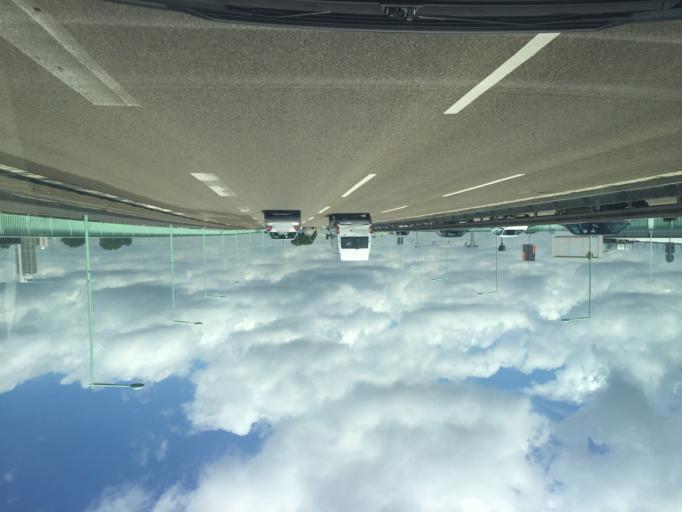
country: DE
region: North Rhine-Westphalia
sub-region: Regierungsbezirk Koln
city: Deutz
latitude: 50.9479
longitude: 6.9851
